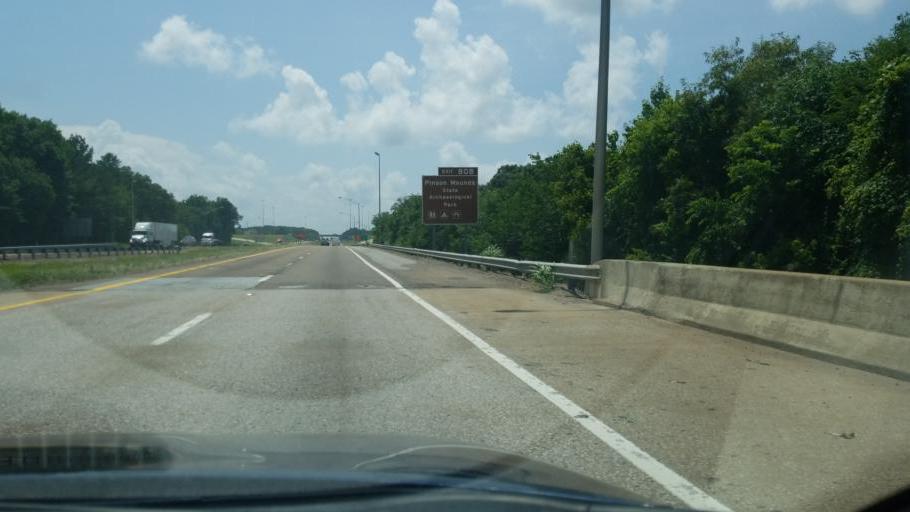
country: US
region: Tennessee
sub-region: Madison County
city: Jackson
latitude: 35.6762
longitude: -88.7986
